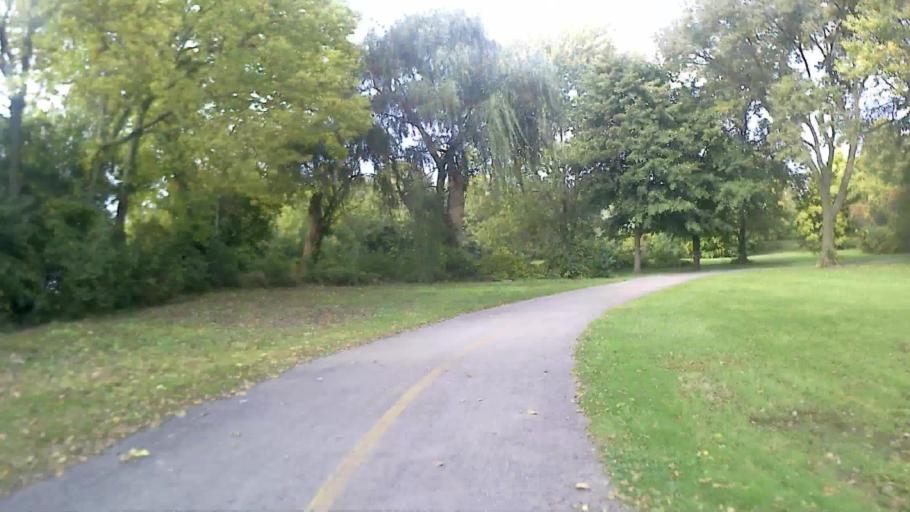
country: US
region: Illinois
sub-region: Kane County
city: Aurora
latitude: 41.7758
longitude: -88.3092
